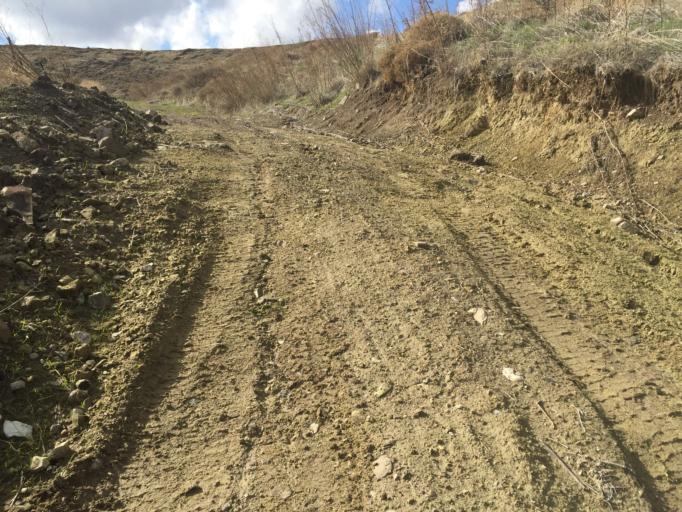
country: CY
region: Limassol
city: Pachna
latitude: 34.8752
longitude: 32.6565
